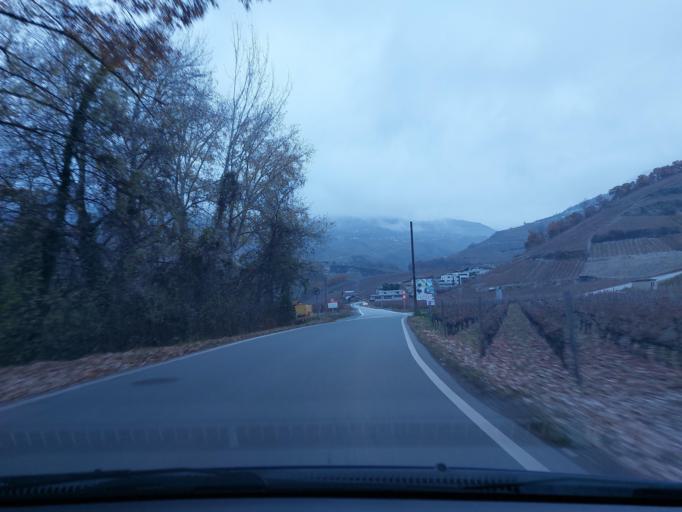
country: CH
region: Valais
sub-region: Conthey District
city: Conthey
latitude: 46.2321
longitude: 7.3126
